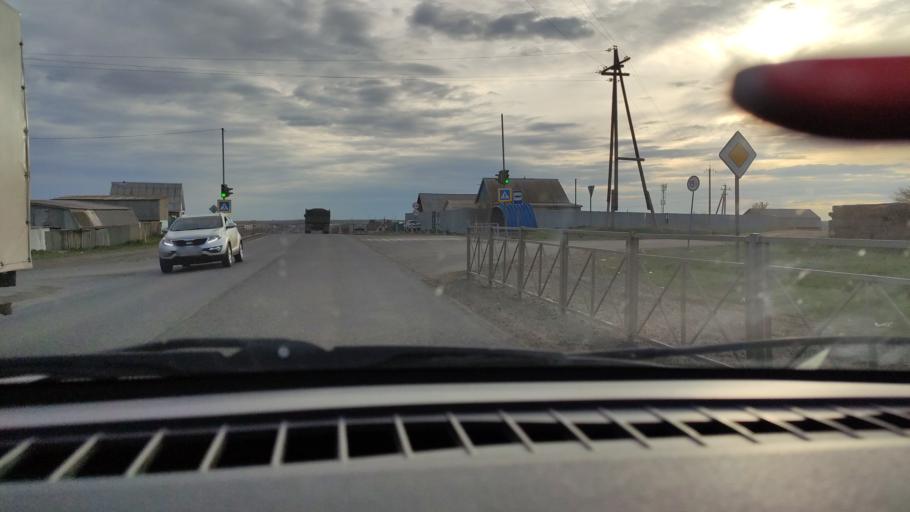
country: RU
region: Orenburg
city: Tatarskaya Kargala
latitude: 51.9489
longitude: 55.1782
